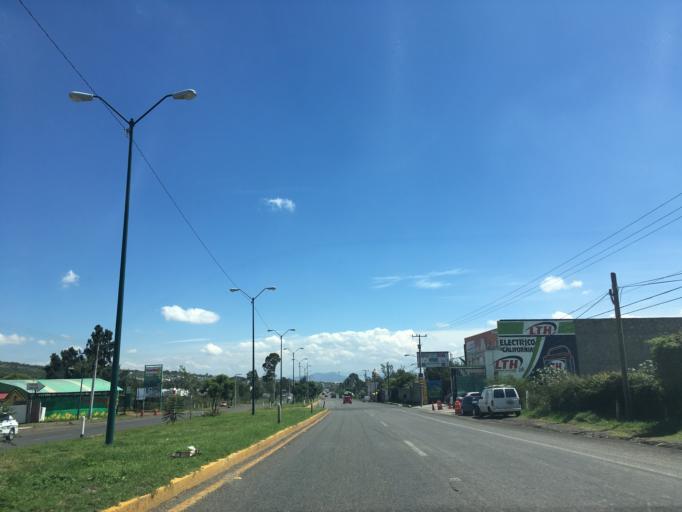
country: MX
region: Michoacan
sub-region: Morelia
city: Villa Magna
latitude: 19.6868
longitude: -101.3172
